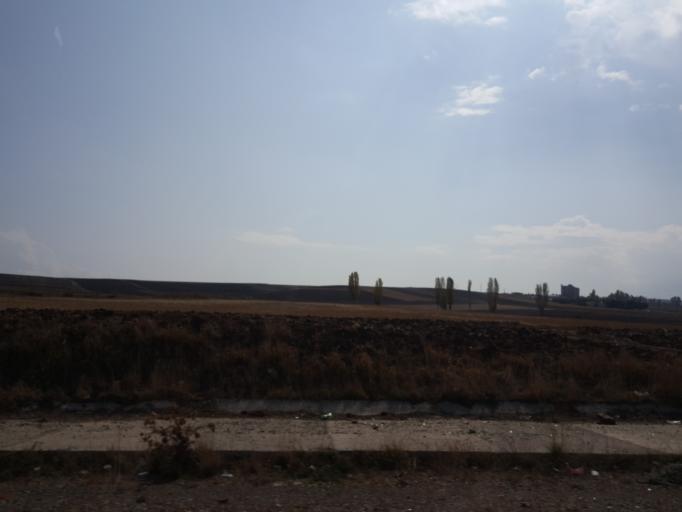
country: TR
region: Corum
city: Alaca
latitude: 40.1541
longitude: 34.8572
